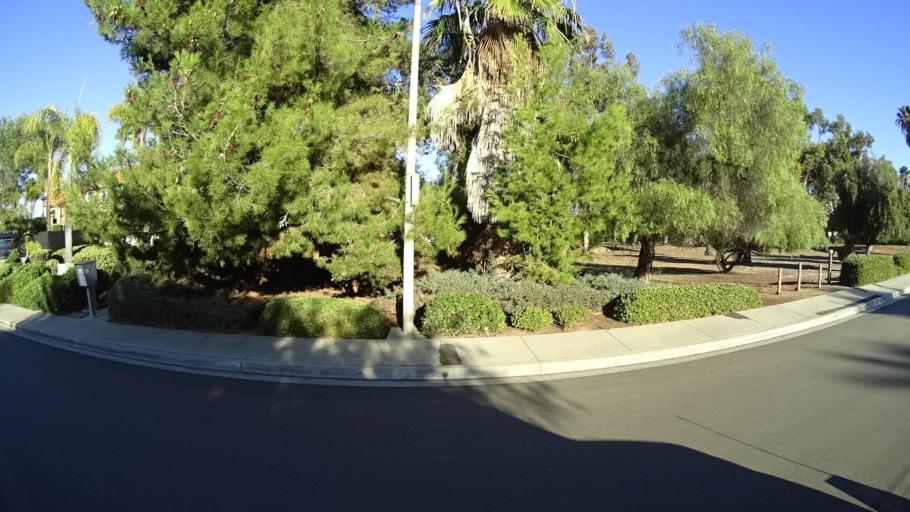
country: US
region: California
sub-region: San Diego County
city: Bonita
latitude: 32.6688
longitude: -117.0409
